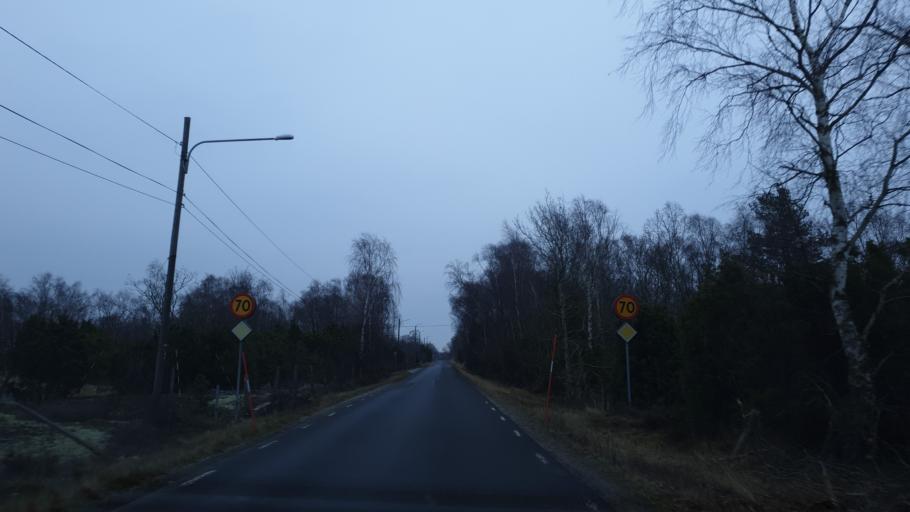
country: SE
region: Blekinge
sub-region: Karlskrona Kommun
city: Karlskrona
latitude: 56.1117
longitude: 15.6132
